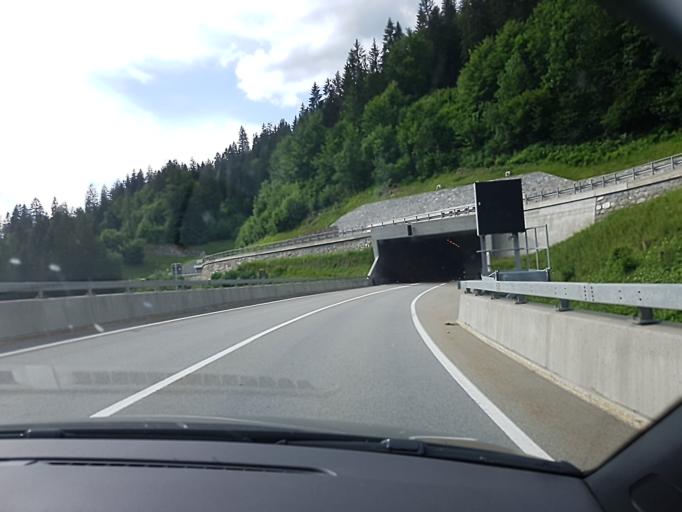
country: CH
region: Grisons
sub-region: Praettigau/Davos District
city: Klosters Serneus
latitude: 46.9024
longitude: 9.8271
